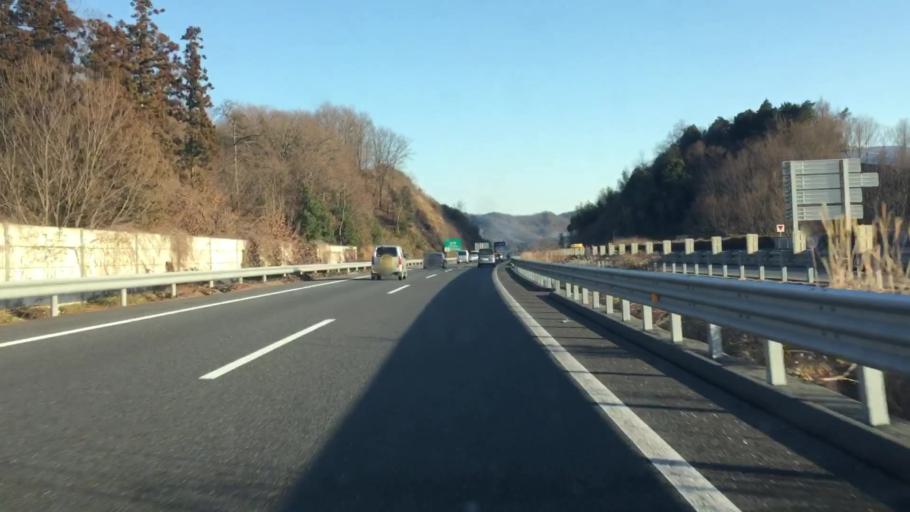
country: JP
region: Tochigi
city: Ashikaga
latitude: 36.3663
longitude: 139.4737
